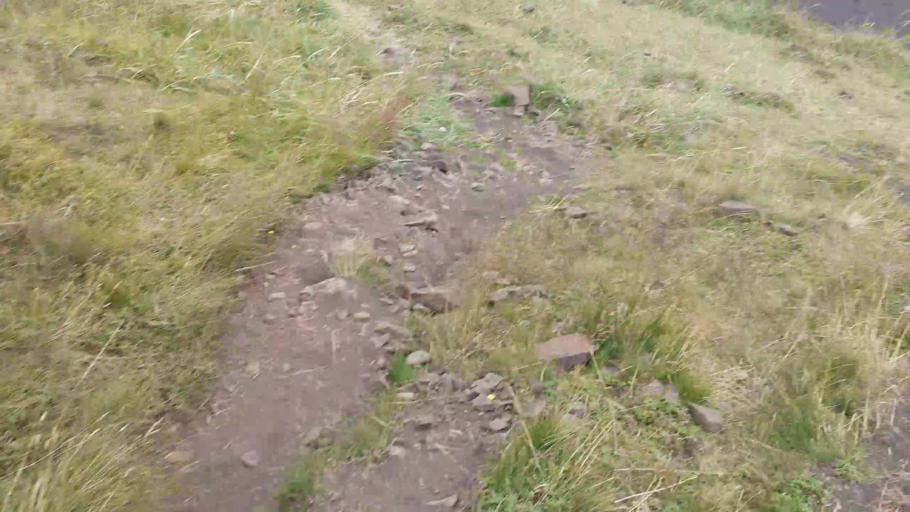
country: IS
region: Northwest
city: Saudarkrokur
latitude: 65.6058
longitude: -20.6369
